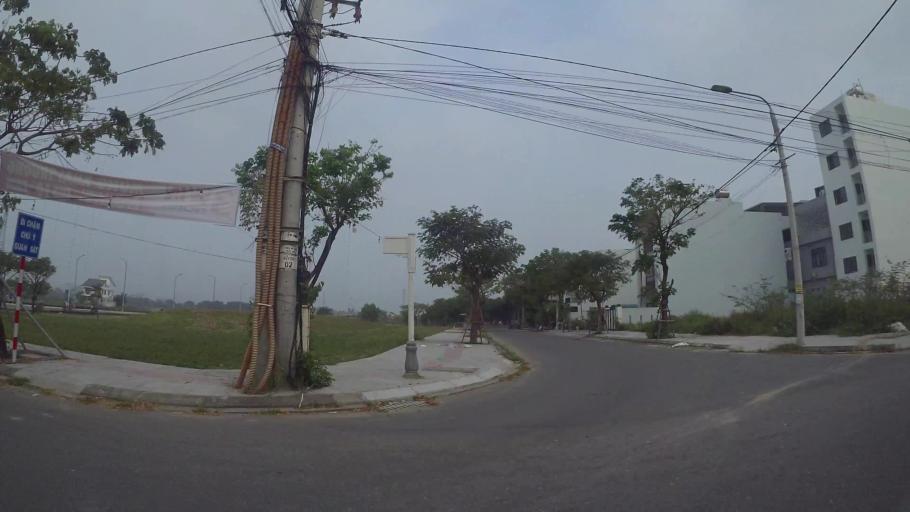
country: VN
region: Da Nang
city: Cam Le
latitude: 16.0232
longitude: 108.2253
